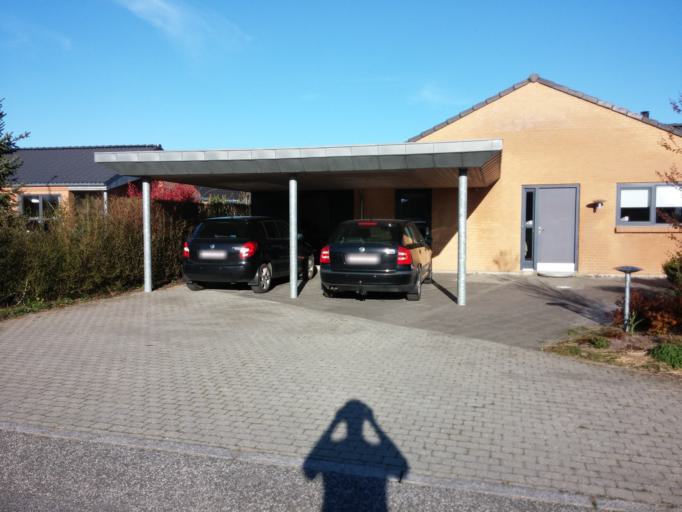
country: DK
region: Central Jutland
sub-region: Arhus Kommune
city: Sabro
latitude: 56.2091
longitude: 10.0428
